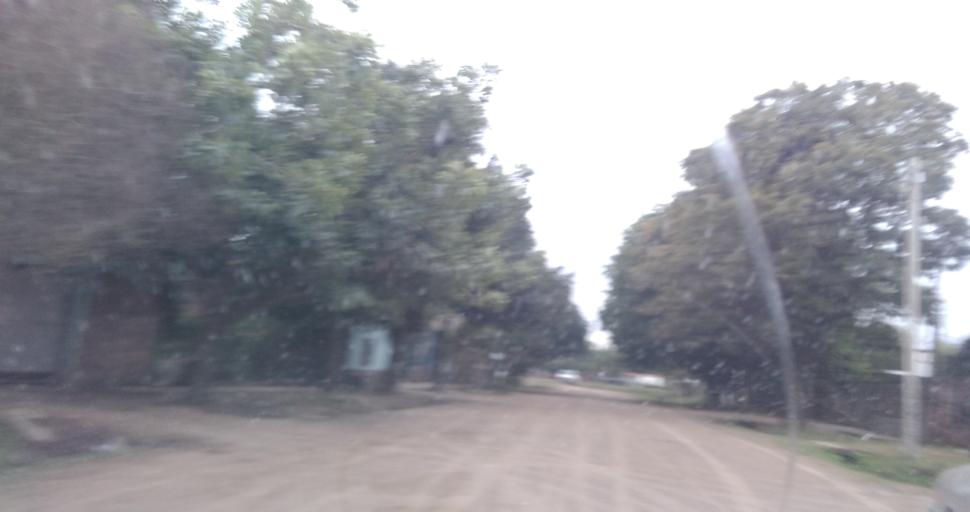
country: AR
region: Chaco
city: Fontana
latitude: -27.4322
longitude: -59.0187
